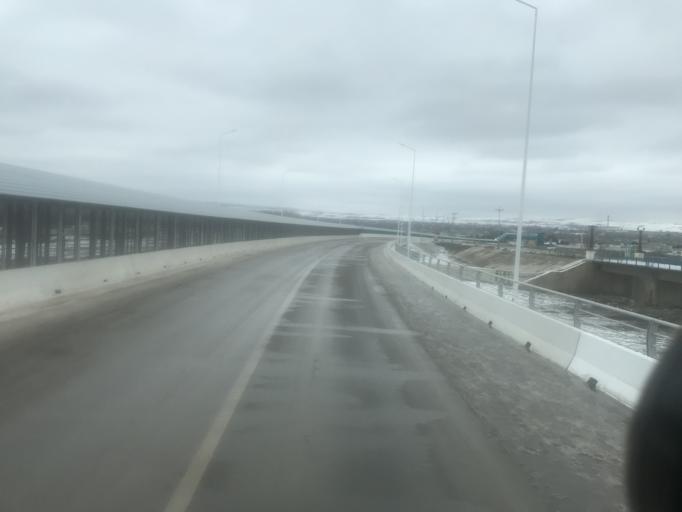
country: AZ
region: Qusar
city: Samur
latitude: 41.6369
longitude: 48.4160
